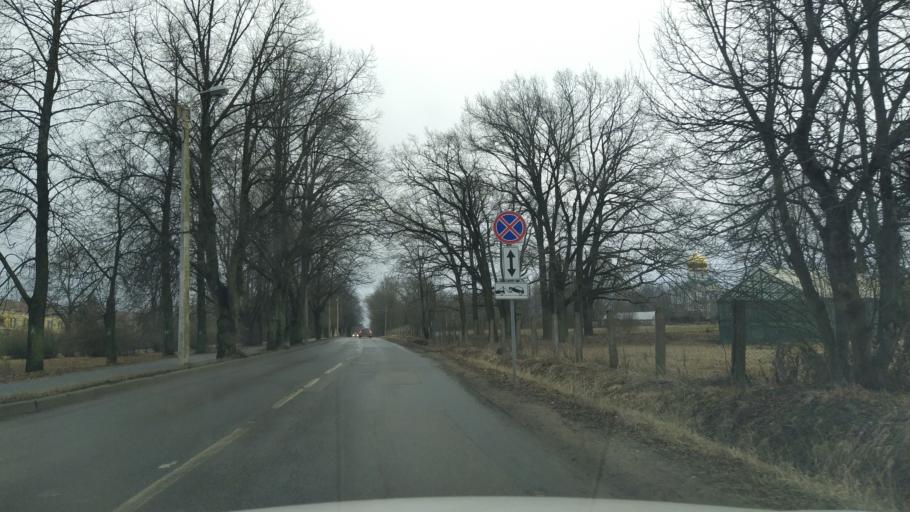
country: RU
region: St.-Petersburg
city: Pushkin
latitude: 59.7285
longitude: 30.3876
